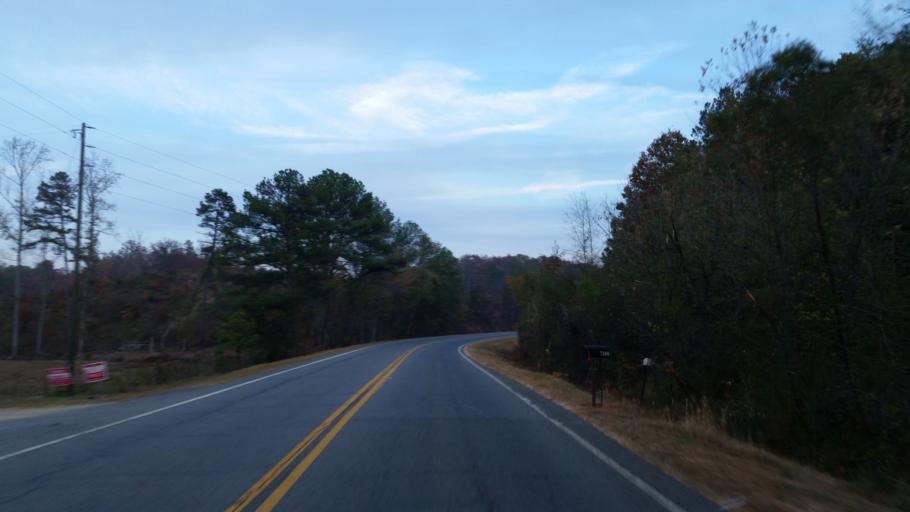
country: US
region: Georgia
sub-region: Murray County
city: Chatsworth
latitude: 34.5914
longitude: -84.7390
